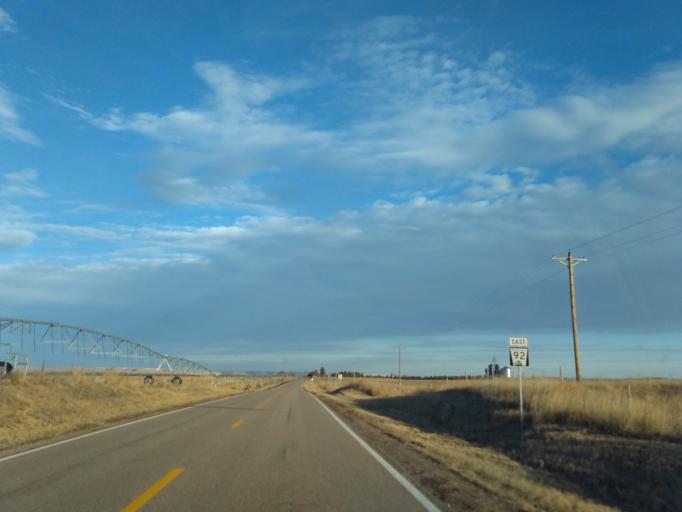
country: US
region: Nebraska
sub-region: Morrill County
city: Bridgeport
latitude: 41.5983
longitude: -102.9633
